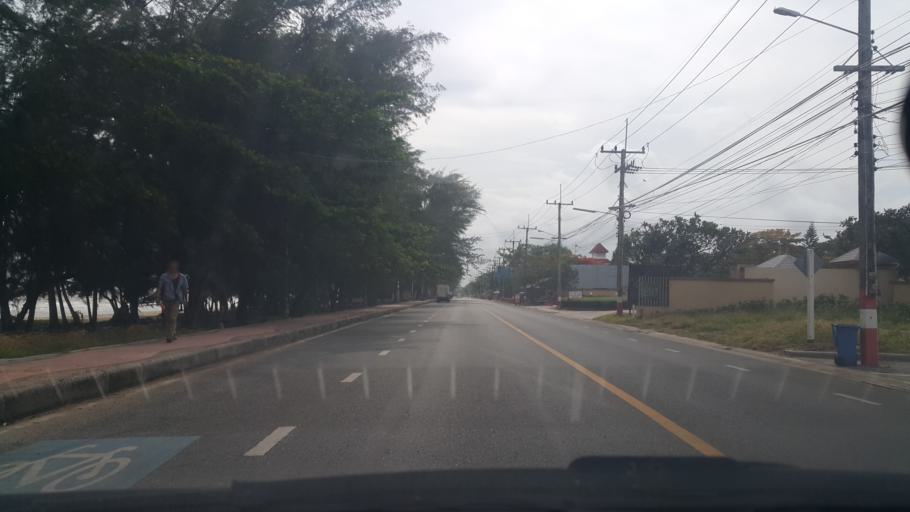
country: TH
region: Rayong
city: Rayong
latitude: 12.6179
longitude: 101.3730
